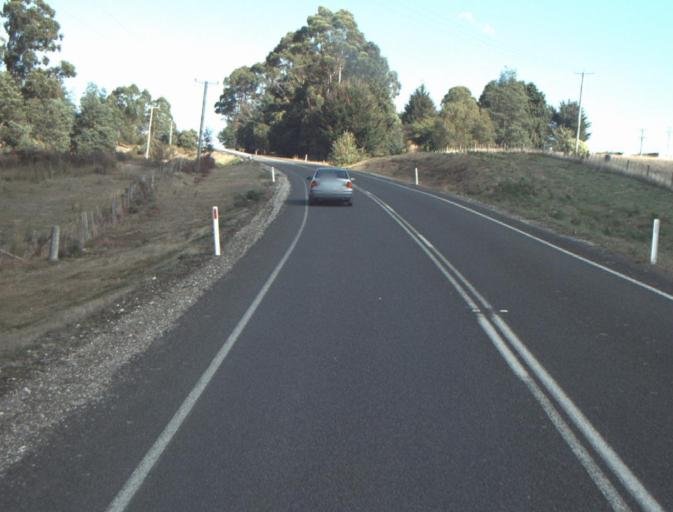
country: AU
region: Tasmania
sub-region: Launceston
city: Mayfield
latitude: -41.2822
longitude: 147.2189
